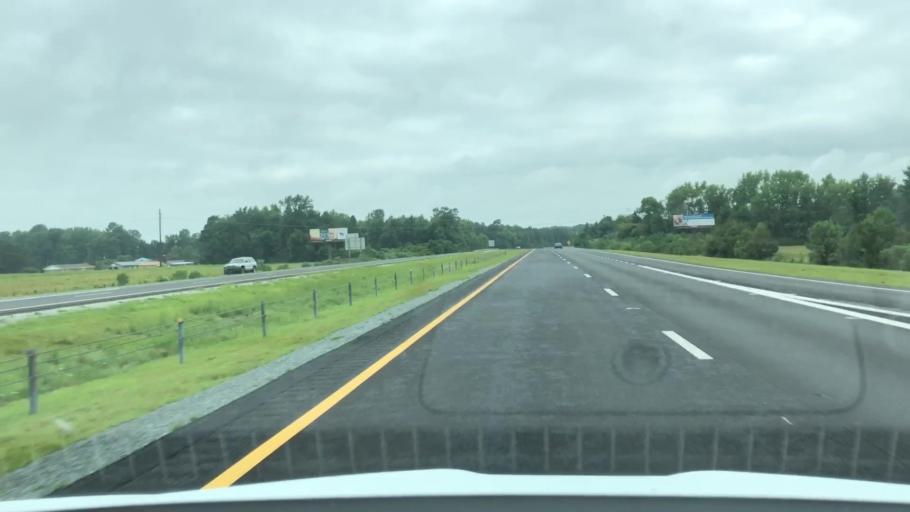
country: US
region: North Carolina
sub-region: Wayne County
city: Fremont
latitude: 35.4981
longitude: -77.9976
